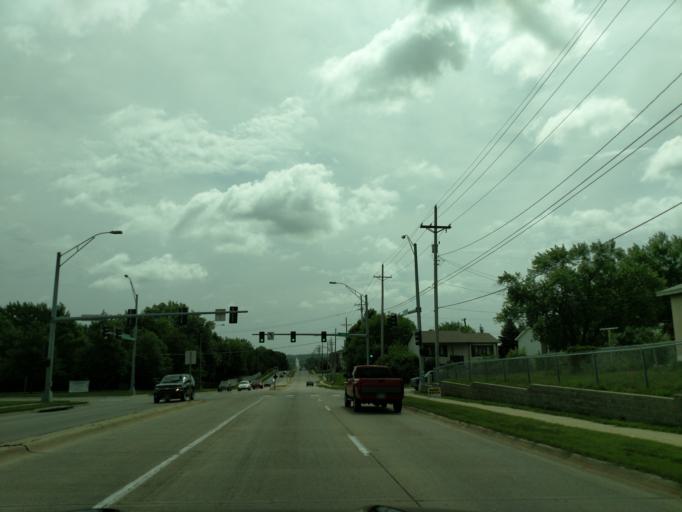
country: US
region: Nebraska
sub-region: Sarpy County
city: La Vista
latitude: 41.1908
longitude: -96.0337
